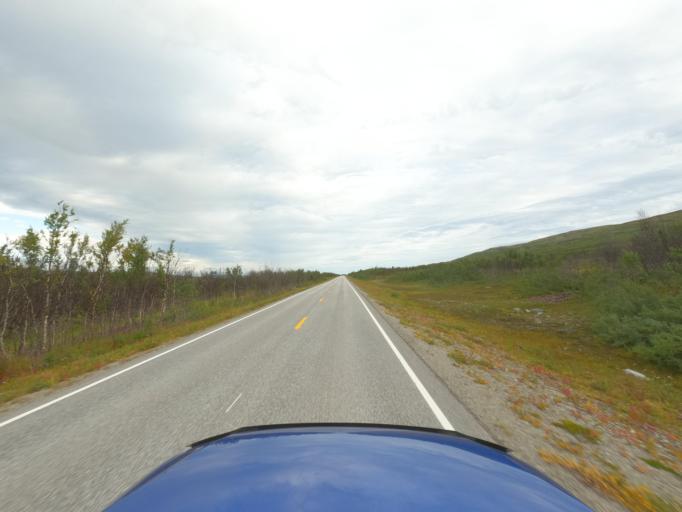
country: NO
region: Finnmark Fylke
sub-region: Porsanger
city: Lakselv
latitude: 70.4633
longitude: 24.7726
